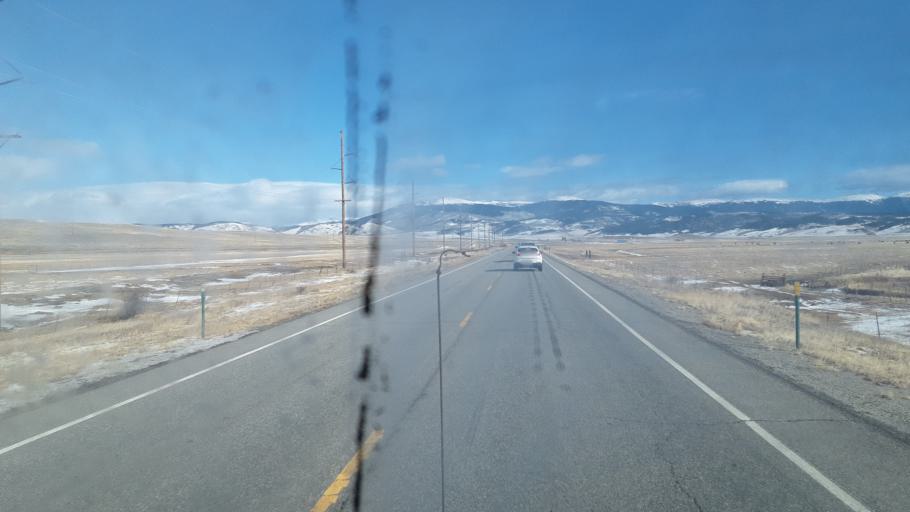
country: US
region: Colorado
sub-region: Park County
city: Fairplay
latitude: 39.3505
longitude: -105.8323
